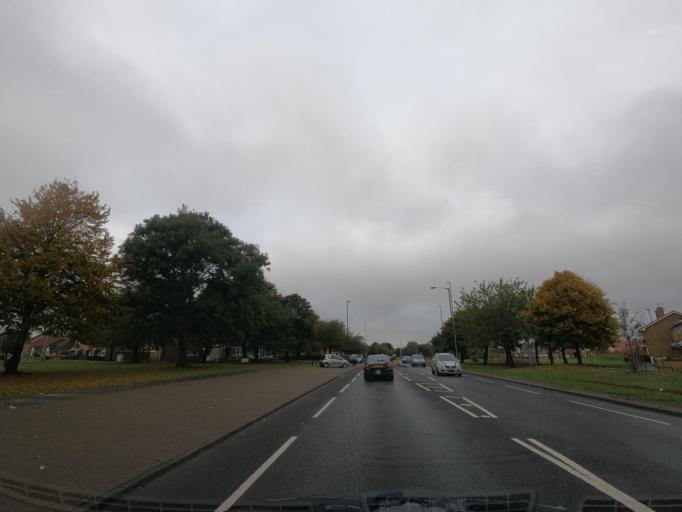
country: GB
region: England
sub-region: Middlesbrough
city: Nunthorpe
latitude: 54.5548
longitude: -1.1851
